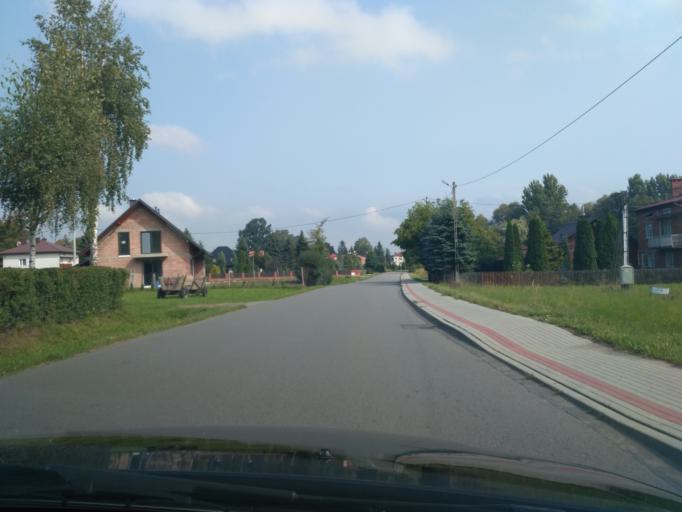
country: PL
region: Subcarpathian Voivodeship
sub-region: Powiat rzeszowski
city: Niechobrz
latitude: 49.9868
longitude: 21.8751
